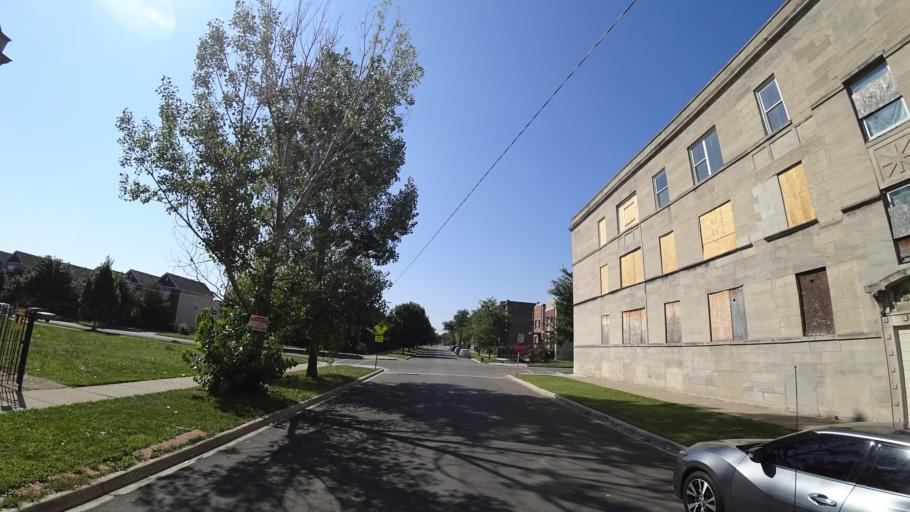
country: US
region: Illinois
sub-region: Cook County
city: Cicero
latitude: 41.8655
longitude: -87.7130
